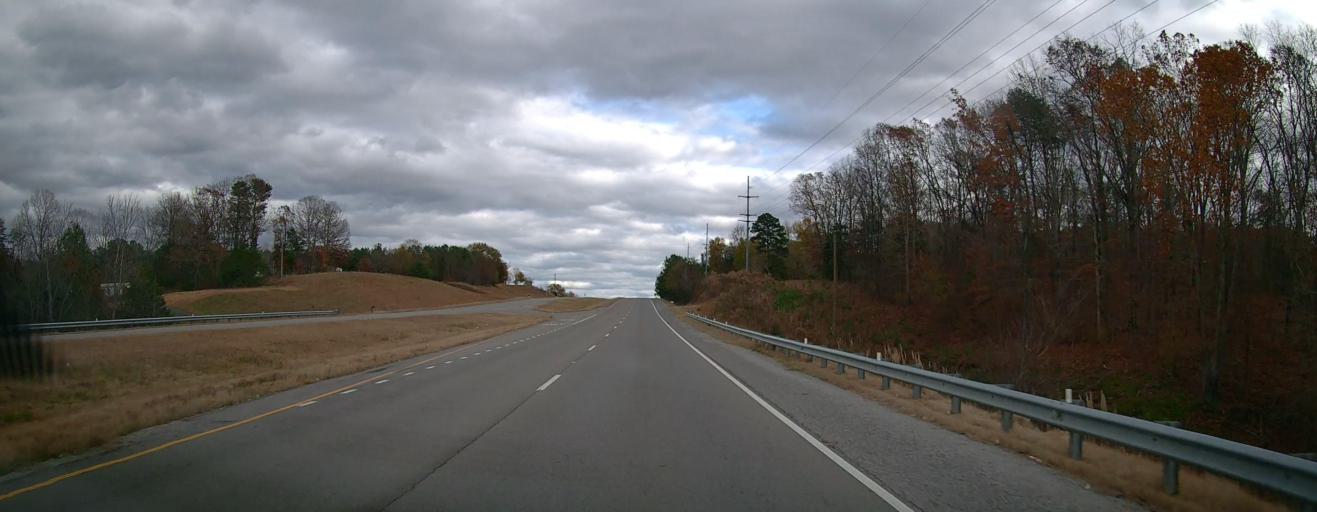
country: US
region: Alabama
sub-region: Lawrence County
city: Moulton
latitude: 34.5638
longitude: -87.3590
